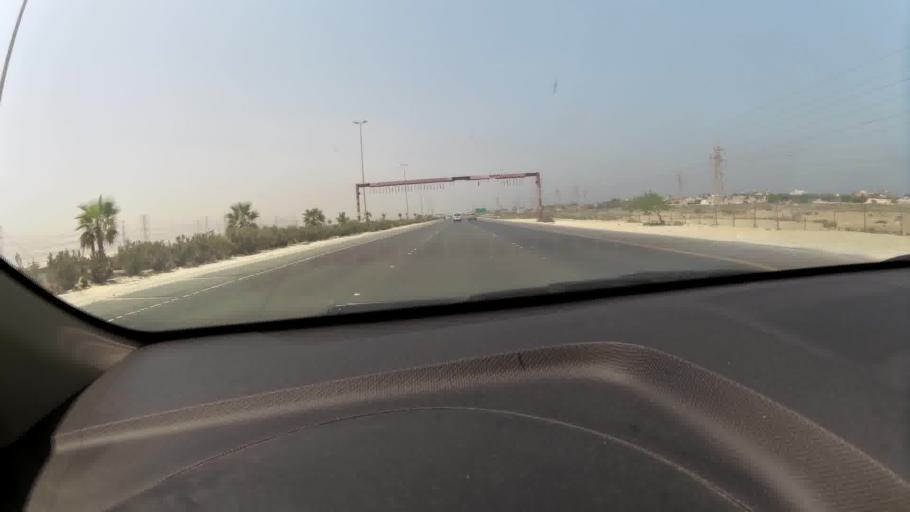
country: KW
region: Al Ahmadi
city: Al Fahahil
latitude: 28.9038
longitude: 48.2174
